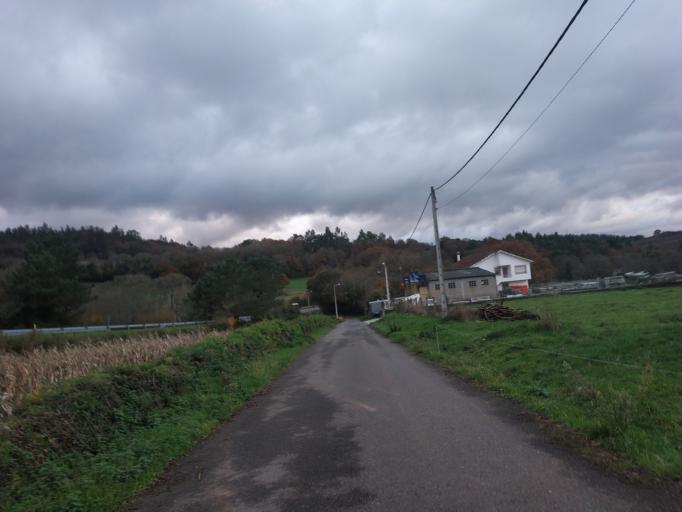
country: ES
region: Galicia
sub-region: Provincia de Pontevedra
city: Silleda
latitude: 42.7824
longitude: -8.1716
